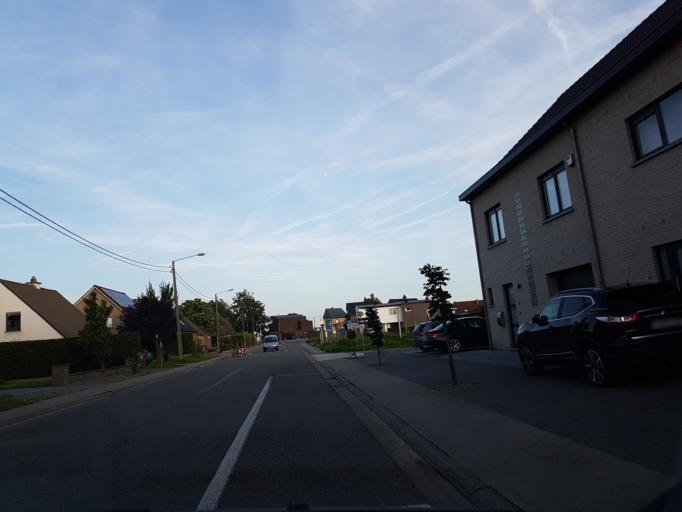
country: BE
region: Flanders
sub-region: Provincie Vlaams-Brabant
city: Merchtem
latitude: 50.9803
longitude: 4.2296
